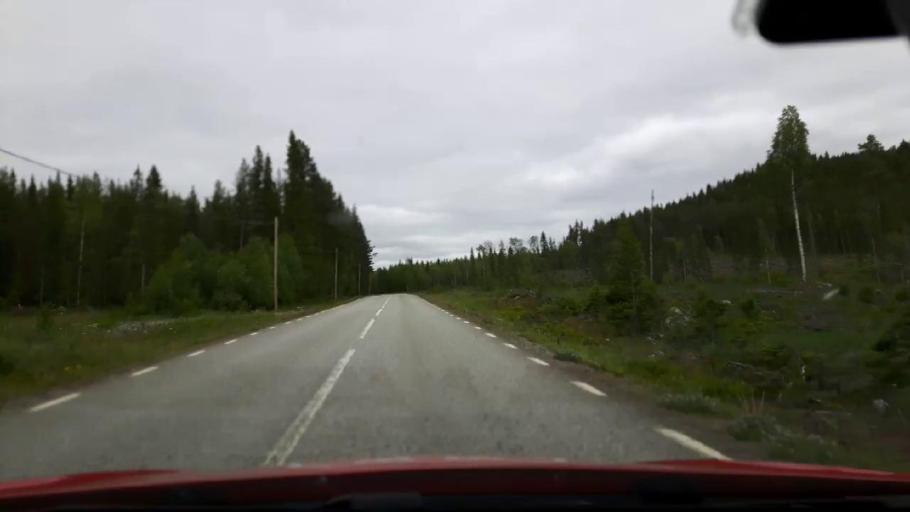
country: SE
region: Jaemtland
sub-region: Stroemsunds Kommun
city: Stroemsund
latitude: 63.3520
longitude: 15.7224
